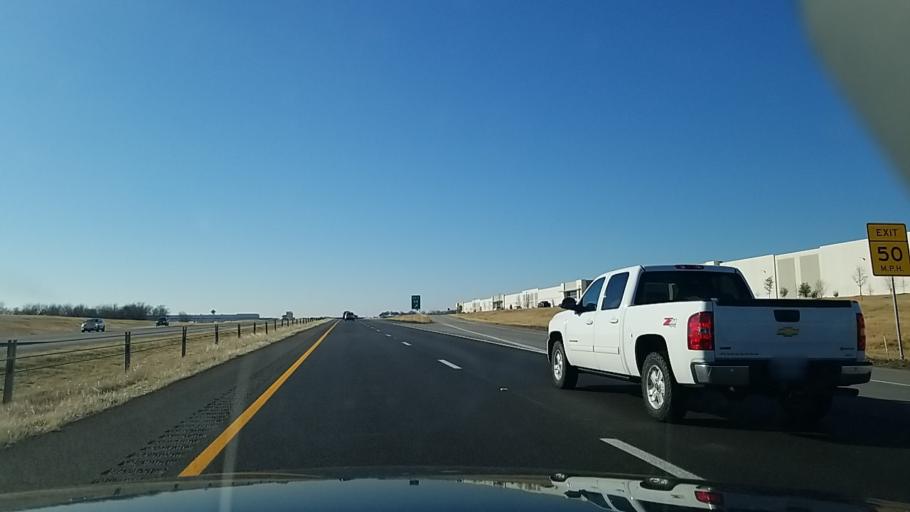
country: US
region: Texas
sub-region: Denton County
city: Roanoke
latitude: 33.0126
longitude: -97.2845
